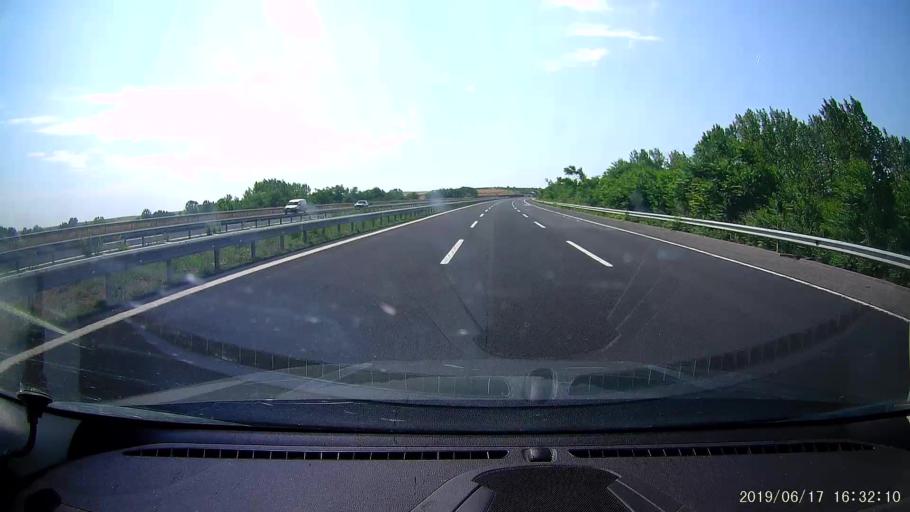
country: TR
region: Kirklareli
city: Buyukkaristiran
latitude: 41.3657
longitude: 27.6067
